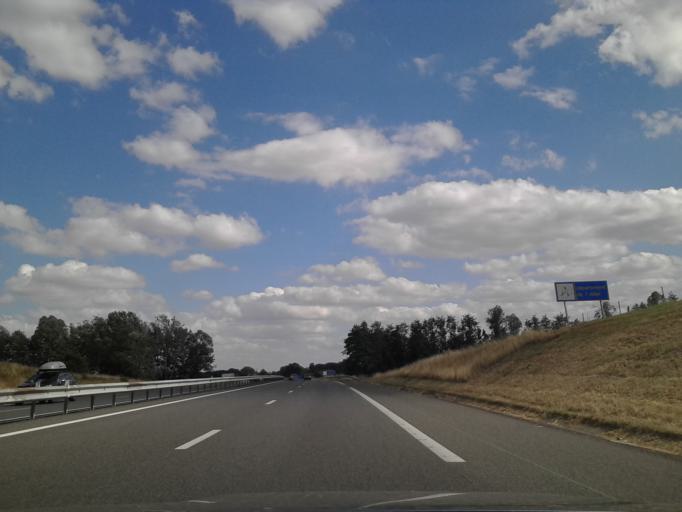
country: FR
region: Auvergne
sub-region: Departement de l'Allier
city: Vallon-en-Sully
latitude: 46.5326
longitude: 2.5598
